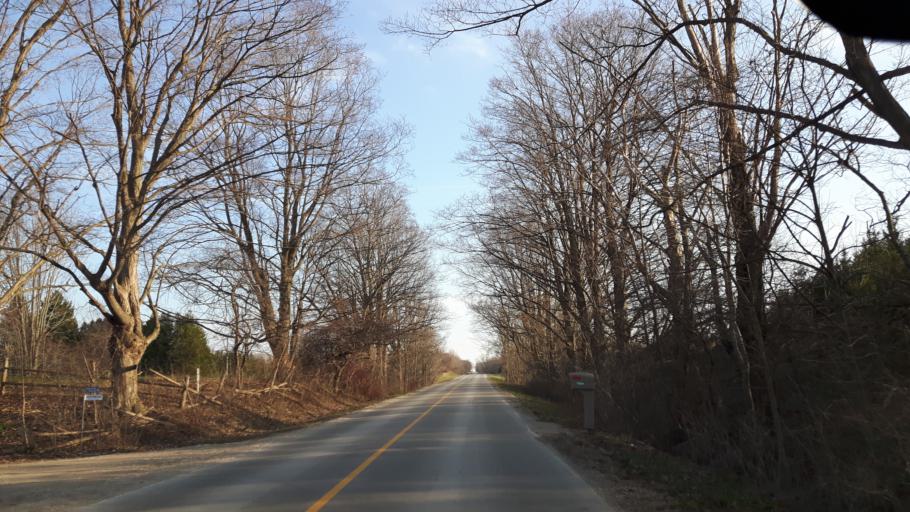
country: CA
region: Ontario
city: Goderich
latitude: 43.6790
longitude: -81.6644
